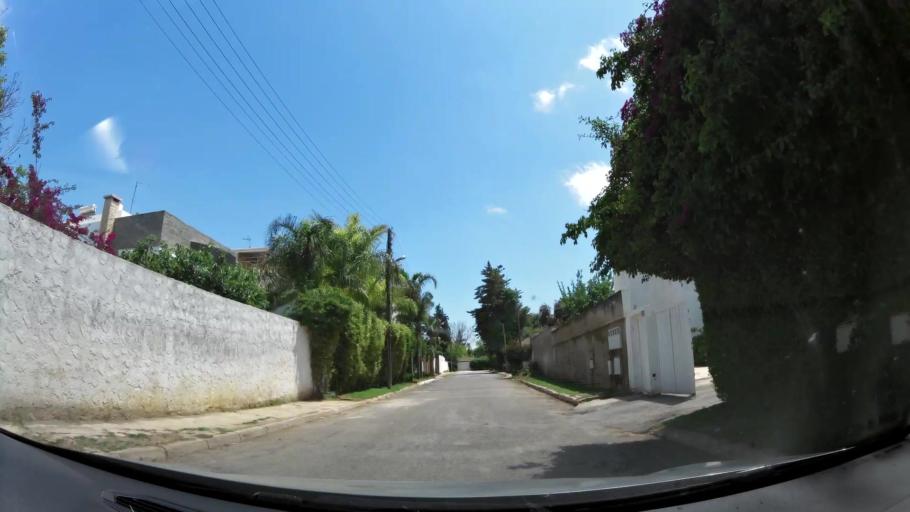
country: MA
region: Fes-Boulemane
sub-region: Fes
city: Fes
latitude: 34.0115
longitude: -4.9915
